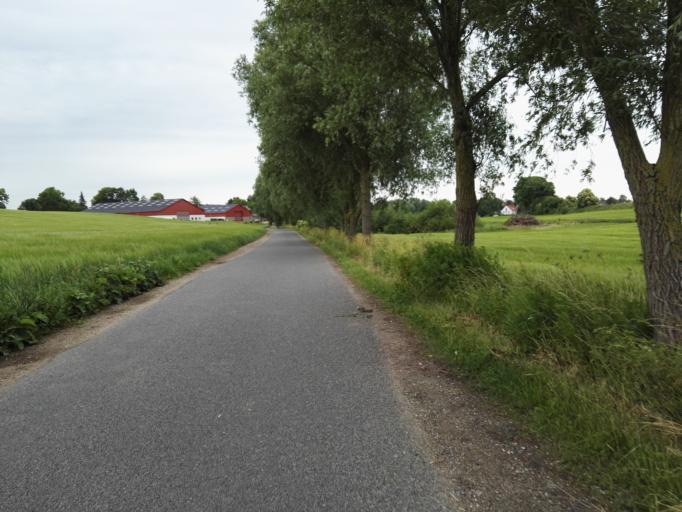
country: DK
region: Zealand
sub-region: Roskilde Kommune
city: Jyllinge
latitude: 55.7946
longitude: 12.1090
